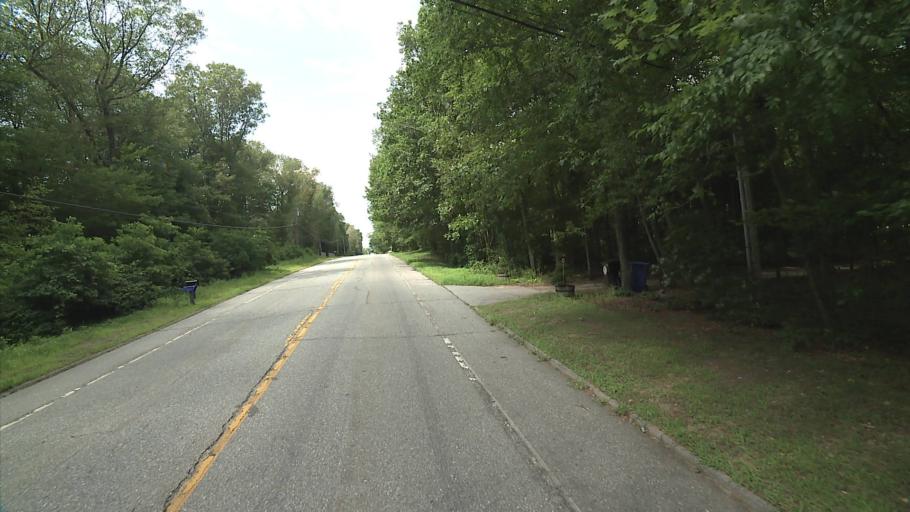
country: US
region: Connecticut
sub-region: New London County
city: Colchester
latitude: 41.5424
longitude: -72.2733
